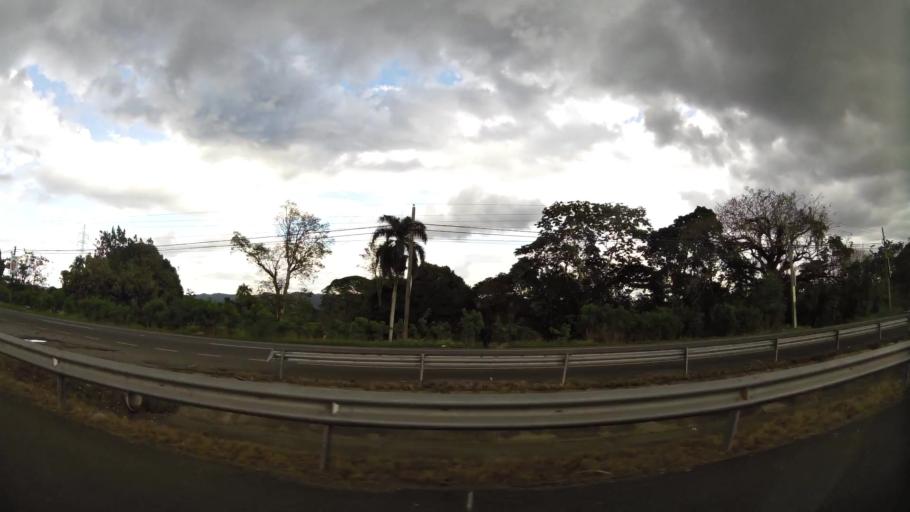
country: DO
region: Monsenor Nouel
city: Sabana del Puerto
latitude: 19.0327
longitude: -70.4454
